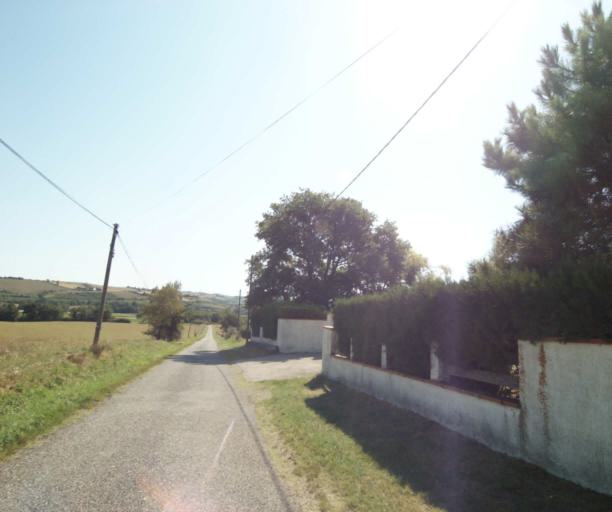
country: FR
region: Midi-Pyrenees
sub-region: Departement de l'Ariege
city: Lezat-sur-Leze
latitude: 43.2986
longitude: 1.3305
